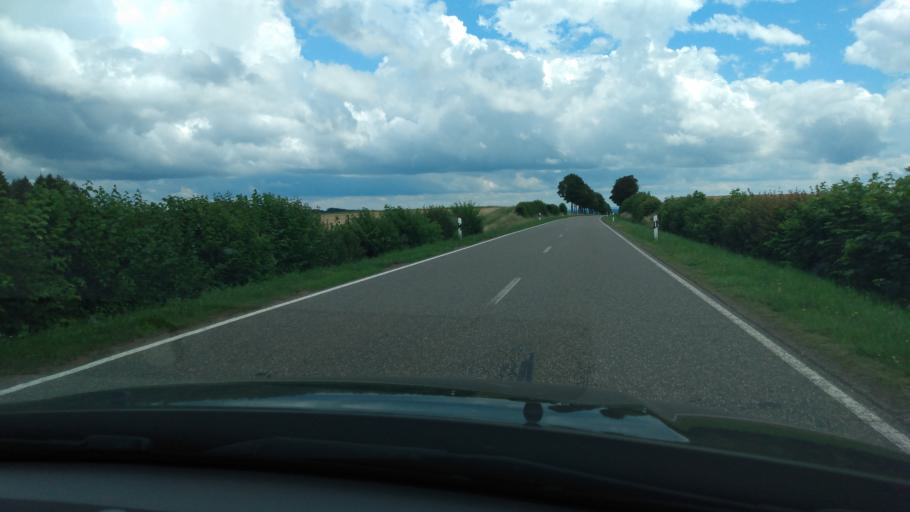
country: DE
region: Rheinland-Pfalz
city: Manderscheid
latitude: 50.1093
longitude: 6.7902
